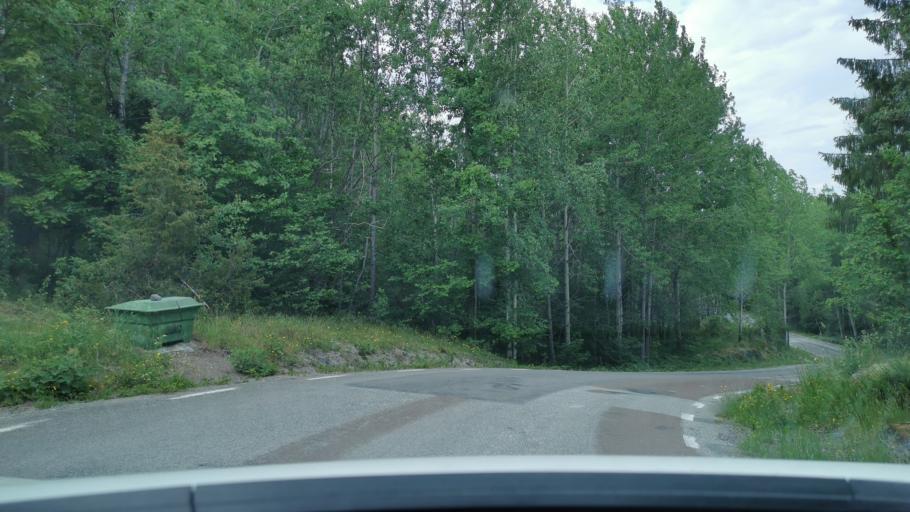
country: SE
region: Vaestra Goetaland
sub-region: Bengtsfors Kommun
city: Dals Langed
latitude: 58.8566
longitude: 12.4035
